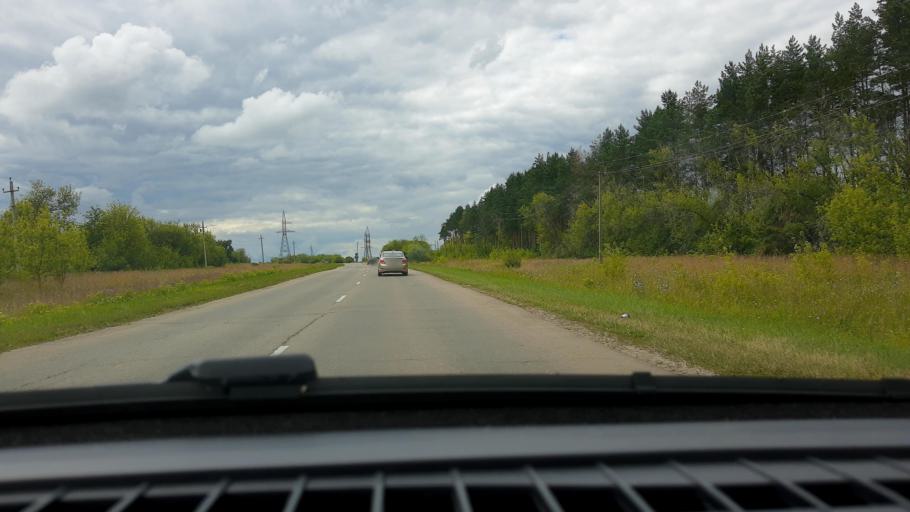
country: RU
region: Nizjnij Novgorod
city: Sergach
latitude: 55.5539
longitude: 45.5916
